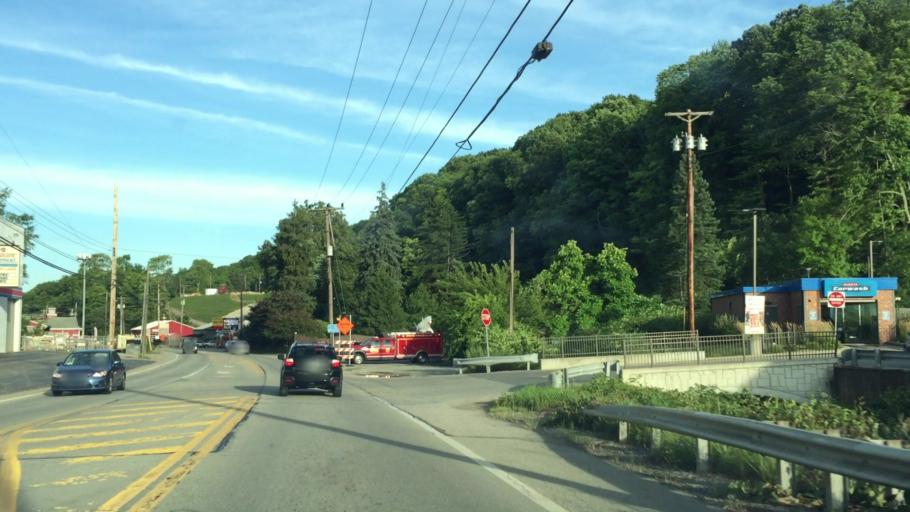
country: US
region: Pennsylvania
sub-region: Allegheny County
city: West View
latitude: 40.5152
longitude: -80.0089
